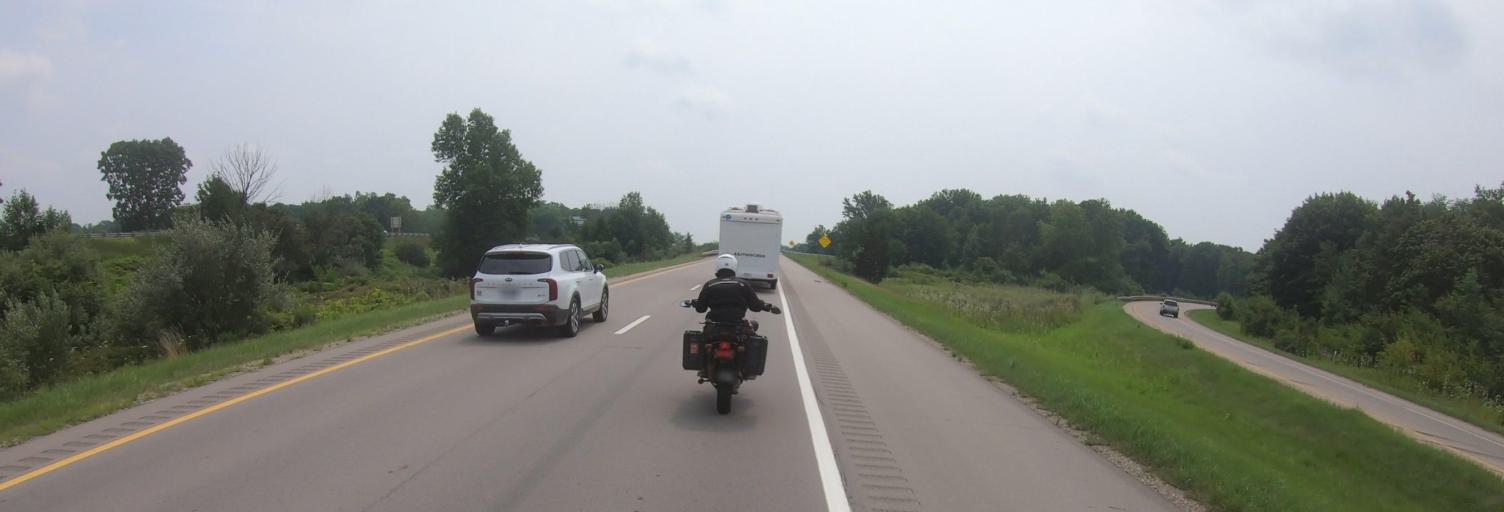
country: US
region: Michigan
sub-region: Ingham County
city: Holt
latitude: 42.6780
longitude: -84.4979
